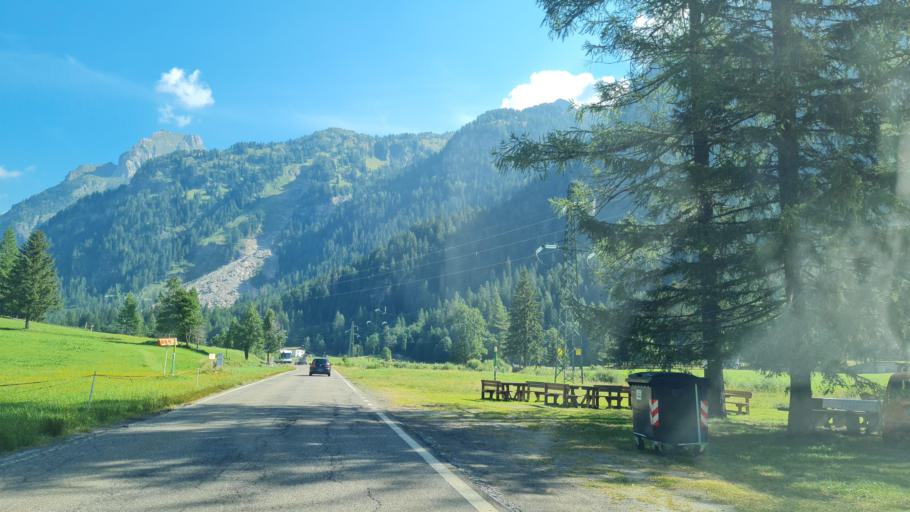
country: IT
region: Piedmont
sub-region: Provincia Verbano-Cusio-Ossola
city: Formazza
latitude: 46.3616
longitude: 8.4290
